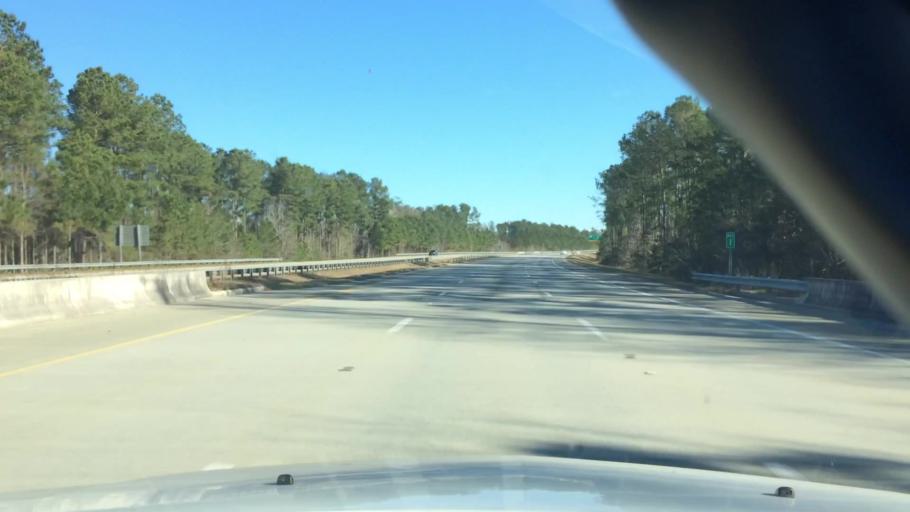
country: US
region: South Carolina
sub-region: Horry County
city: North Myrtle Beach
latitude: 33.8648
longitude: -78.6938
